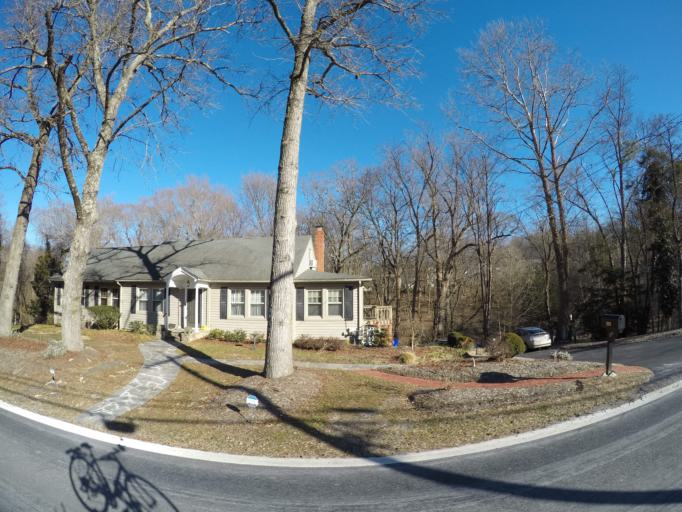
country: US
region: Maryland
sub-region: Howard County
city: Ellicott City
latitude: 39.2630
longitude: -76.7962
